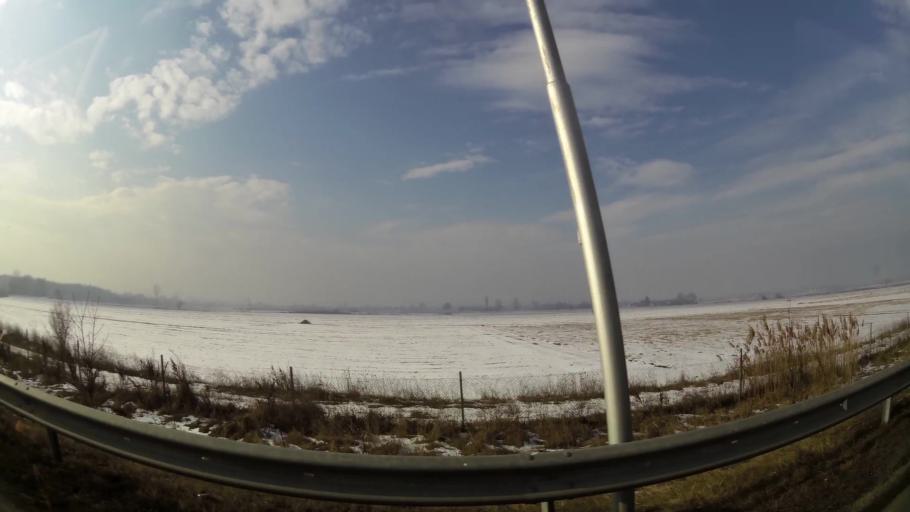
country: MK
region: Ilinden
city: Jurumleri
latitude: 41.9982
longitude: 21.5325
